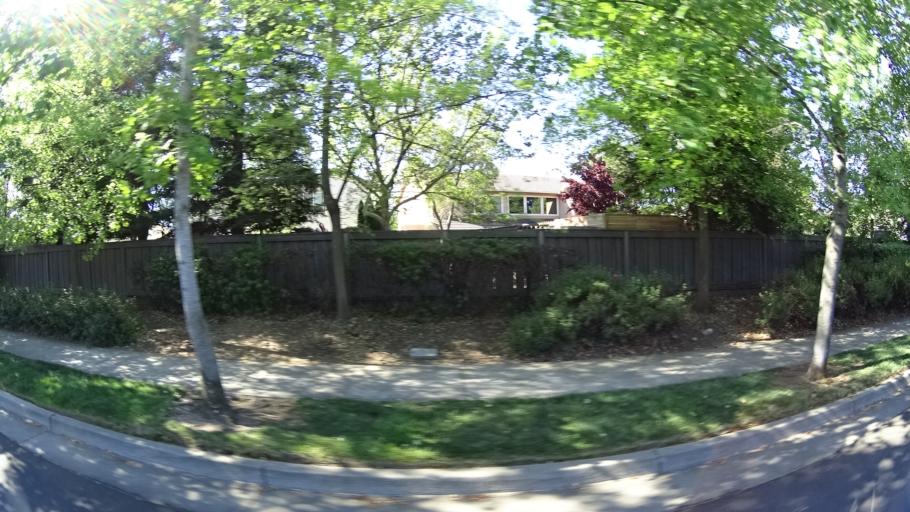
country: US
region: California
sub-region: Placer County
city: Rocklin
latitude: 38.7897
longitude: -121.2736
